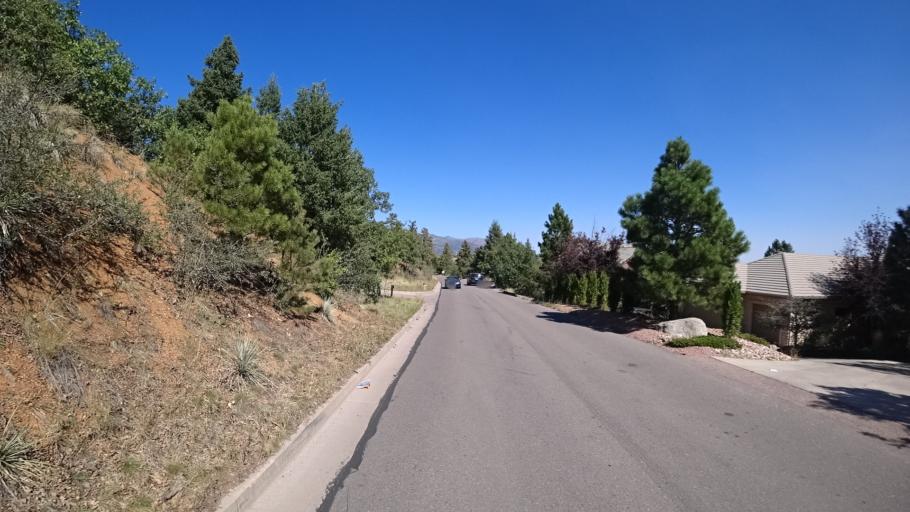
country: US
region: Colorado
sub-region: El Paso County
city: Manitou Springs
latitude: 38.8168
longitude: -104.8816
